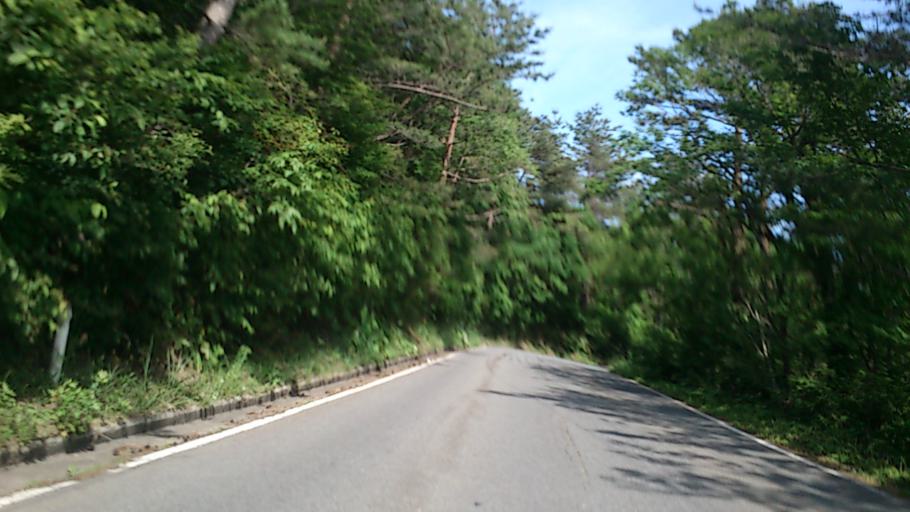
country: JP
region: Aomori
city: Aomori Shi
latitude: 40.7142
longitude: 140.8221
